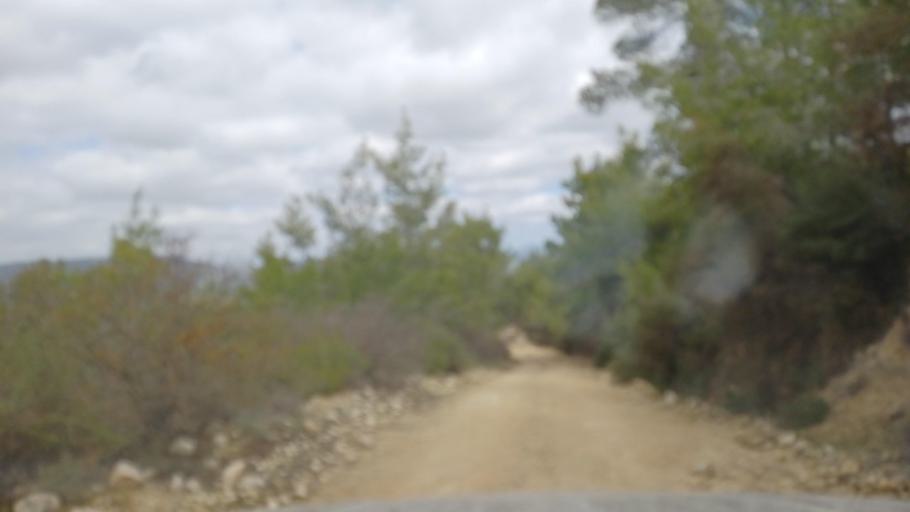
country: CY
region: Limassol
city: Pachna
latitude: 34.7721
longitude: 32.6948
